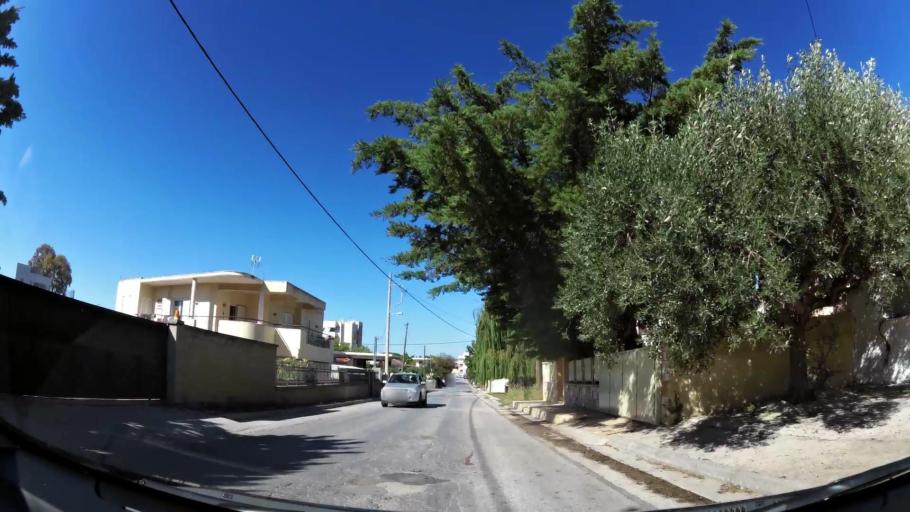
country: GR
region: Attica
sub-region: Nomarchia Anatolikis Attikis
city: Markopoulo
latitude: 37.8776
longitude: 23.9346
